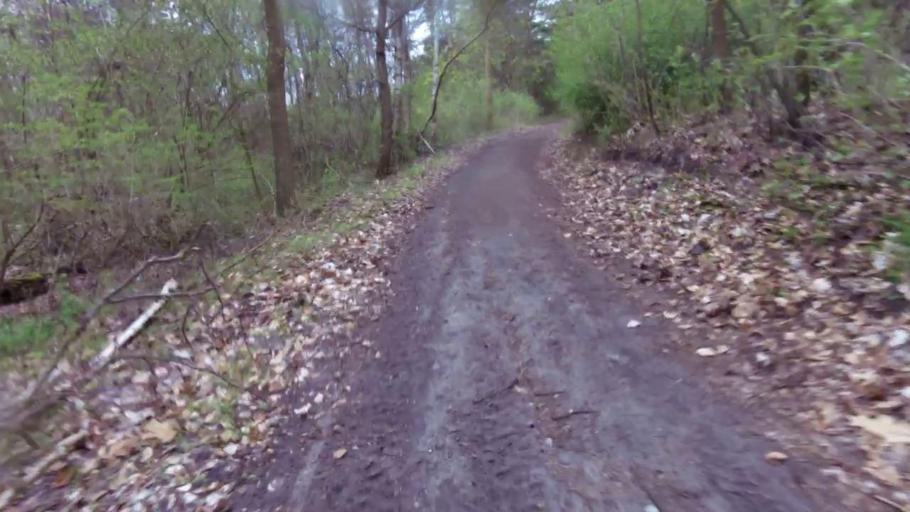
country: PL
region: West Pomeranian Voivodeship
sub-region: Powiat kamienski
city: Dziwnow
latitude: 54.0200
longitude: 14.7289
